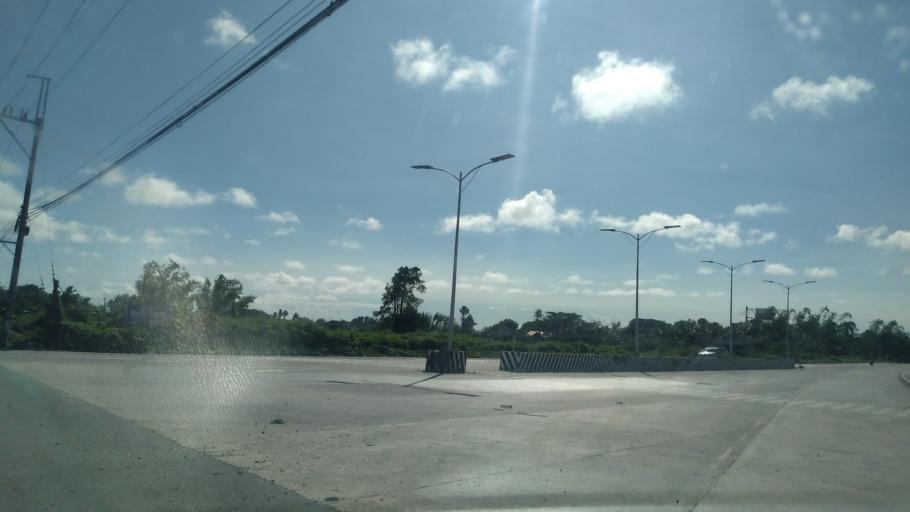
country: PH
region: Calabarzon
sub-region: Province of Quezon
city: Isabang
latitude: 13.9617
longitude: 121.5773
